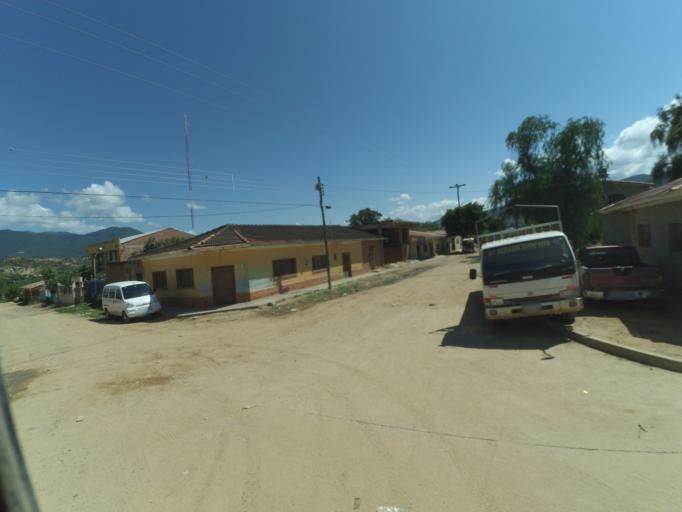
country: BO
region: Santa Cruz
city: Comarapa
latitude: -18.0962
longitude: -64.5872
